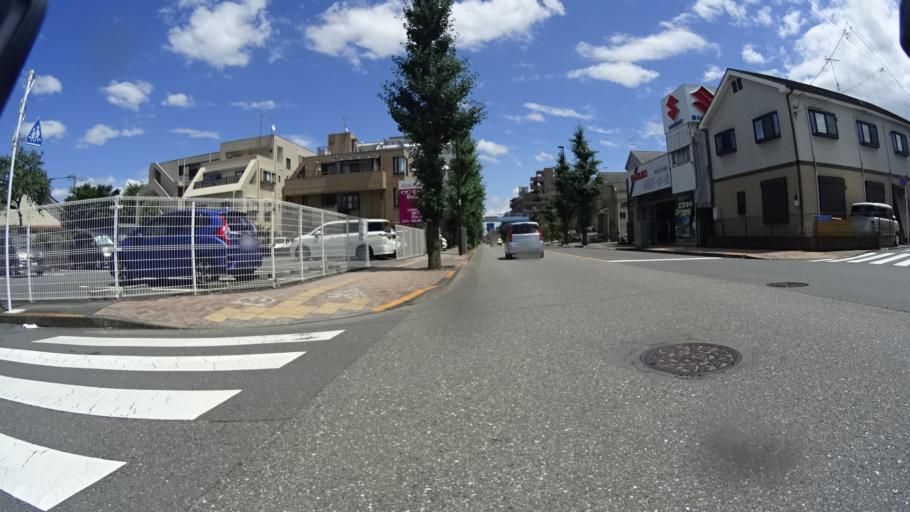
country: JP
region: Tokyo
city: Ome
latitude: 35.7819
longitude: 139.2859
